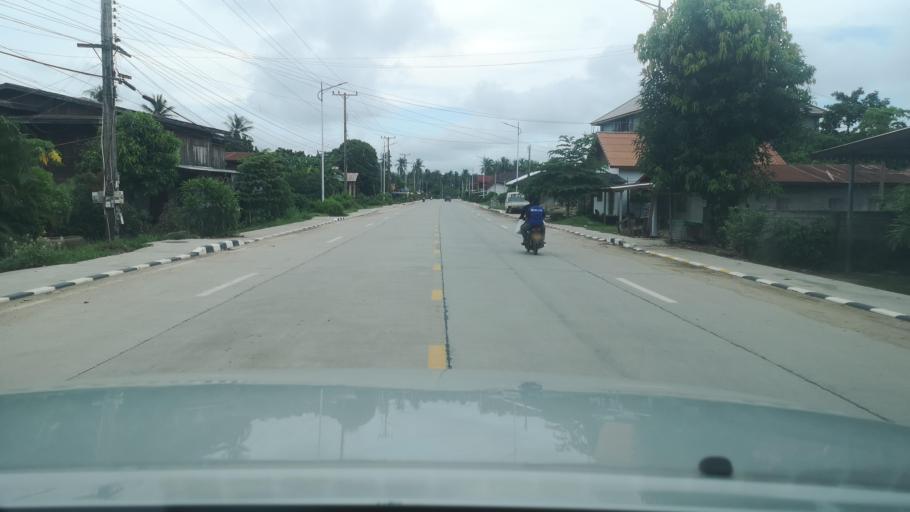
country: TH
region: Nong Khai
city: Tha Bo
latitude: 17.8265
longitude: 102.6547
